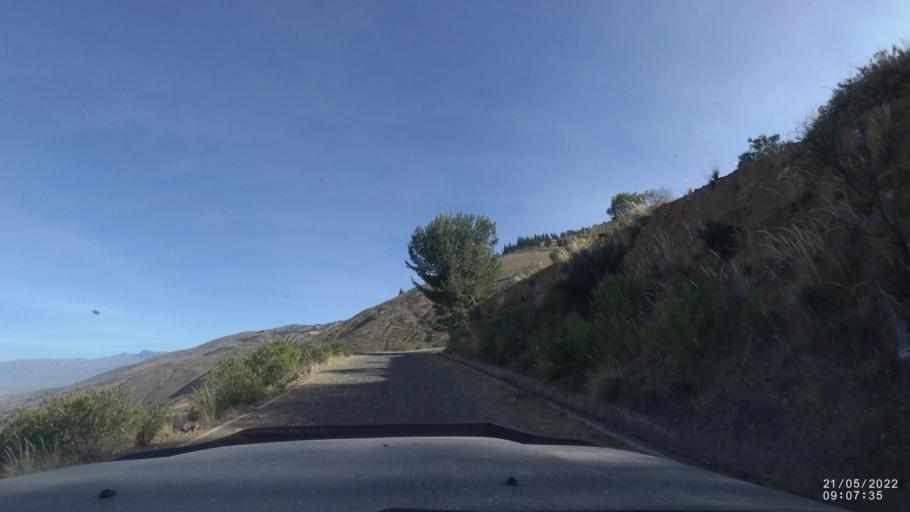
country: BO
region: Cochabamba
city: Cochabamba
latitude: -17.3748
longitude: -66.0265
